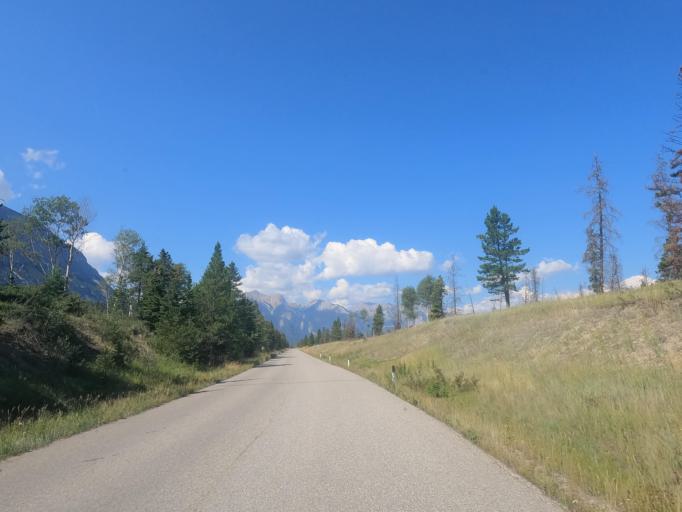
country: CA
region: Alberta
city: Jasper Park Lodge
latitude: 52.9730
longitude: -118.0612
